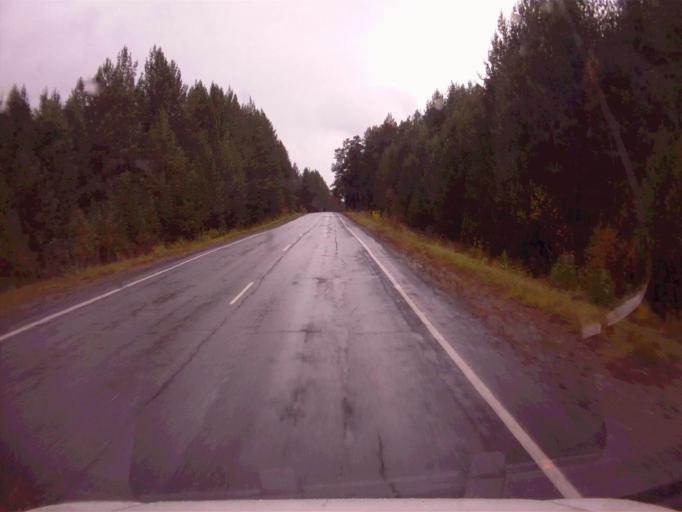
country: RU
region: Chelyabinsk
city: Verkhniy Ufaley
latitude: 56.0202
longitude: 60.3035
